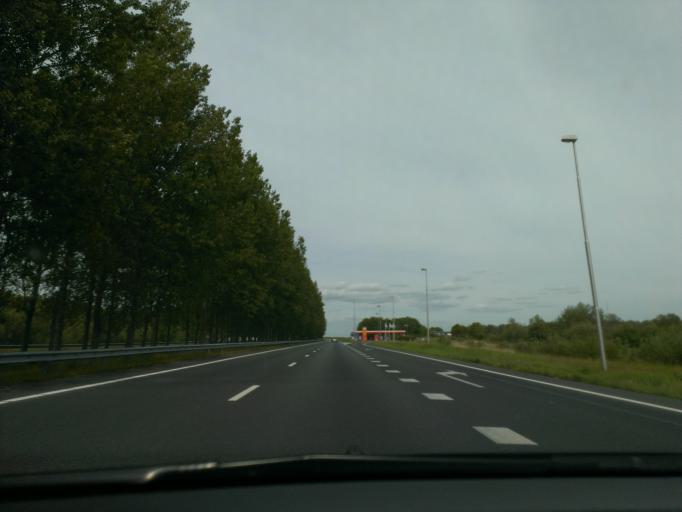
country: NL
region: Flevoland
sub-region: Gemeente Lelystad
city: Lelystad
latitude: 52.4308
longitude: 5.4182
